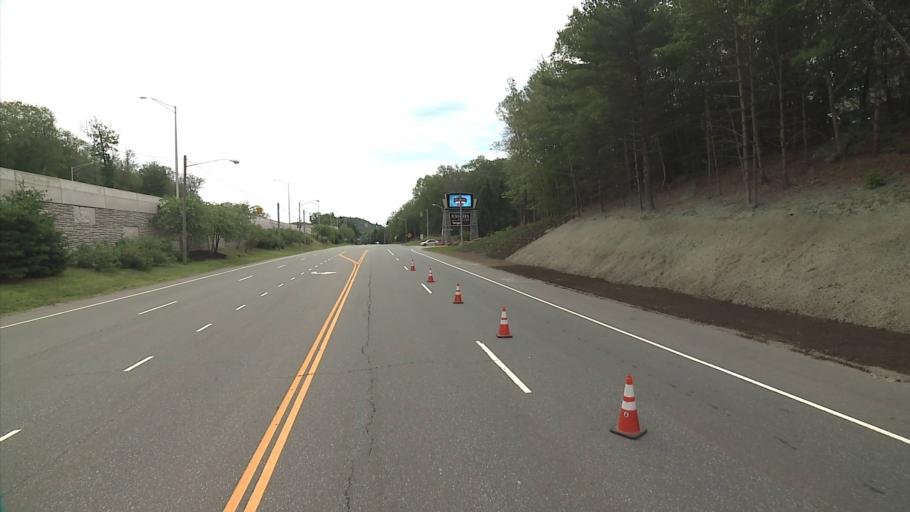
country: US
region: Connecticut
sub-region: New London County
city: Preston City
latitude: 41.4746
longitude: -71.9558
